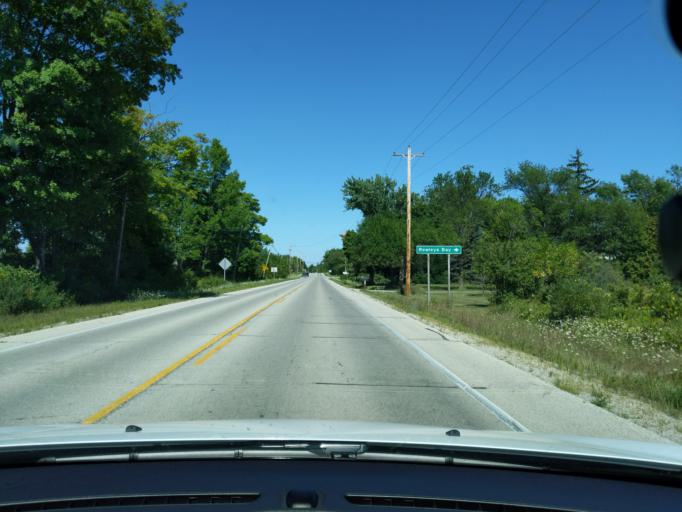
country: US
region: Wisconsin
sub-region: Door County
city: Sturgeon Bay
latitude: 45.2131
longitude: -87.1132
